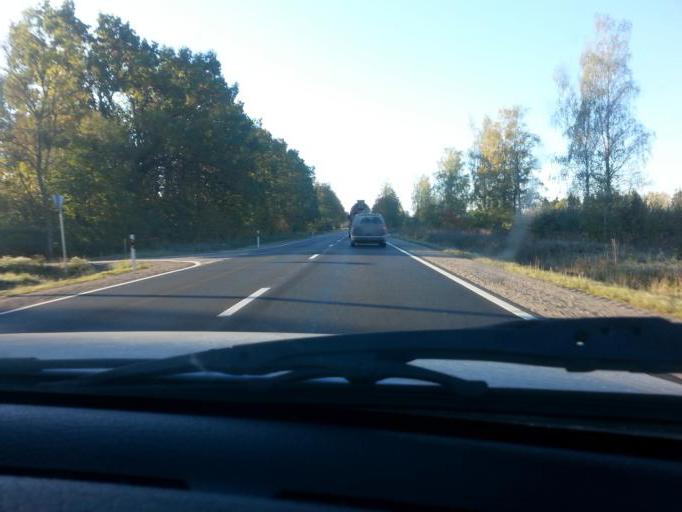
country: LV
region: Jelgava
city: Jelgava
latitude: 56.5090
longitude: 23.7015
